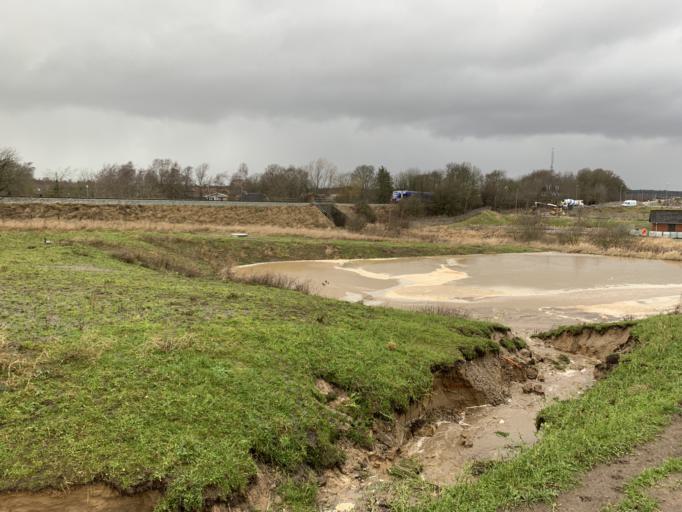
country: DK
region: North Denmark
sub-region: Rebild Kommune
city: Stovring
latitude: 56.8891
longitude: 9.8460
